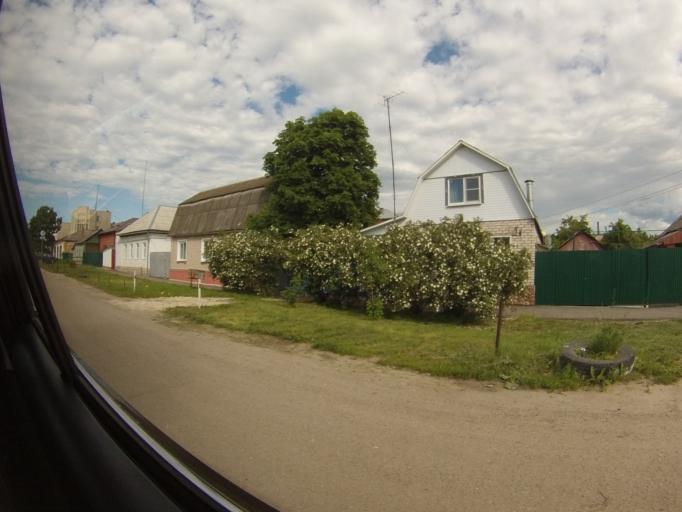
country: RU
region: Orjol
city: Mtsensk
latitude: 53.2766
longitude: 36.5684
